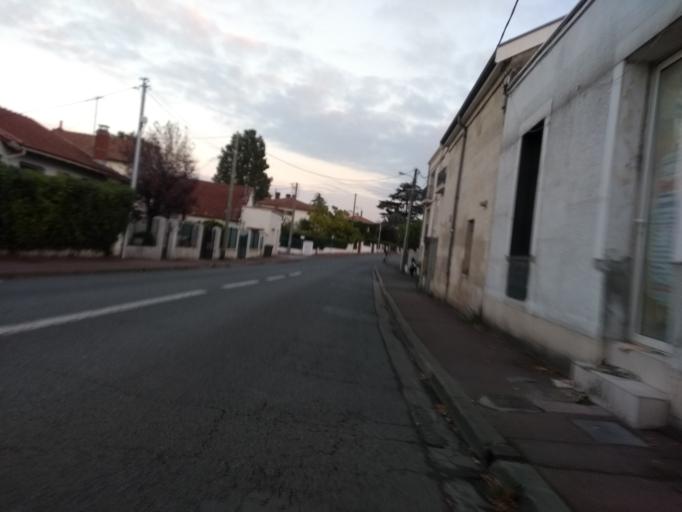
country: FR
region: Aquitaine
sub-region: Departement de la Gironde
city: Talence
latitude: 44.8065
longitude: -0.5857
